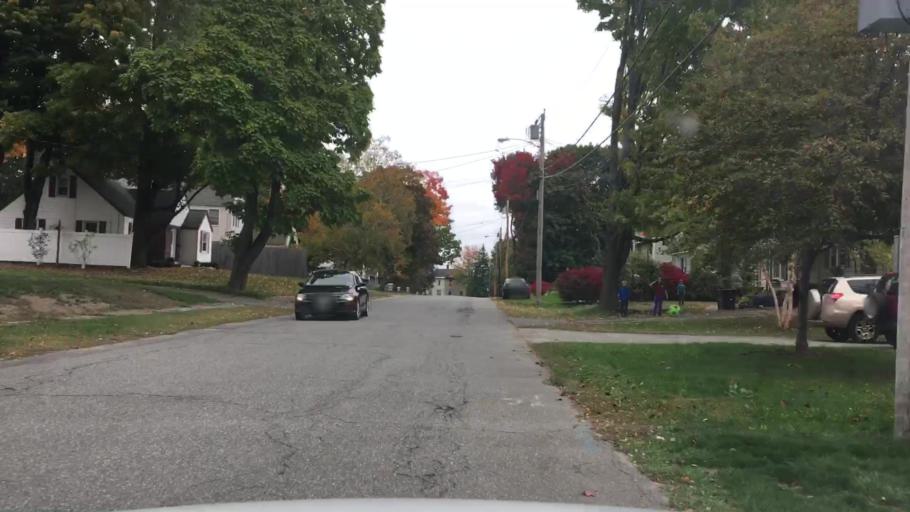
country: US
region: Maine
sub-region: Kennebec County
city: Waterville
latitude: 44.5619
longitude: -69.6381
